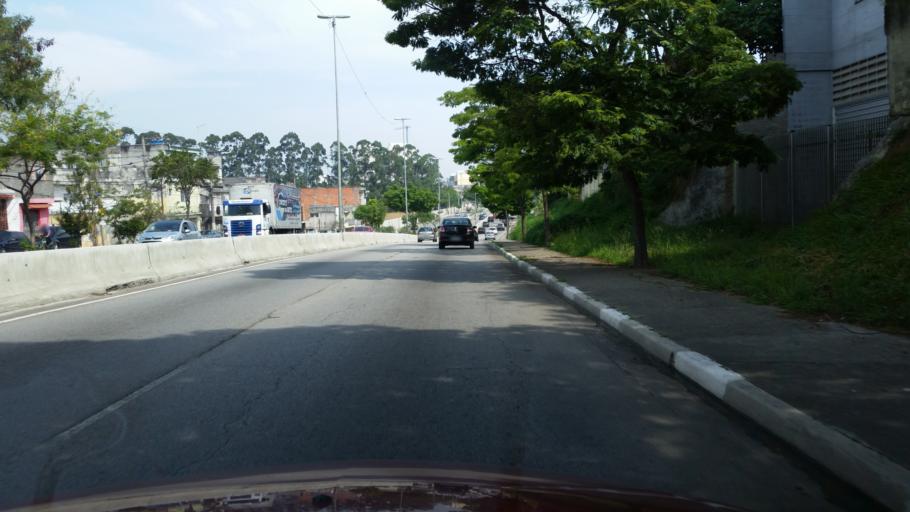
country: BR
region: Sao Paulo
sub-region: Ferraz De Vasconcelos
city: Ferraz de Vasconcelos
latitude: -23.5303
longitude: -46.4306
